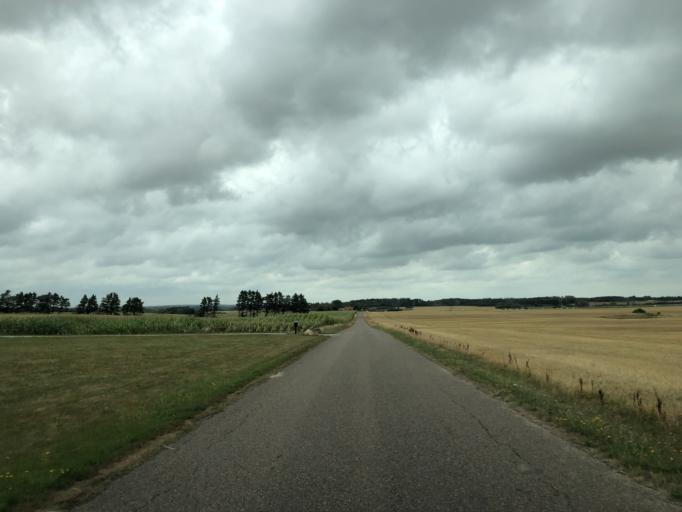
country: DK
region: Central Jutland
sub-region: Ringkobing-Skjern Kommune
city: Skjern
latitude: 56.0904
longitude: 8.4770
